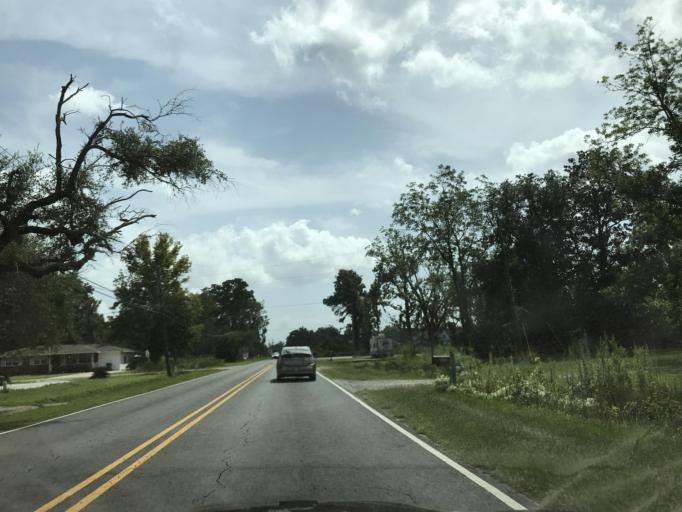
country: US
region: North Carolina
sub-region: New Hanover County
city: Wrightsboro
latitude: 34.2802
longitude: -77.9236
